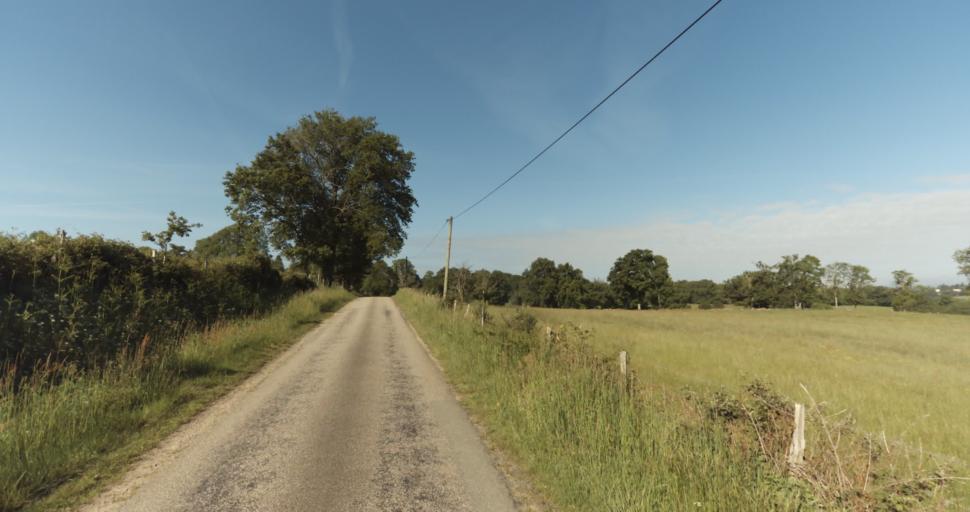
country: FR
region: Limousin
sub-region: Departement de la Haute-Vienne
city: Bosmie-l'Aiguille
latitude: 45.7241
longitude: 1.2367
